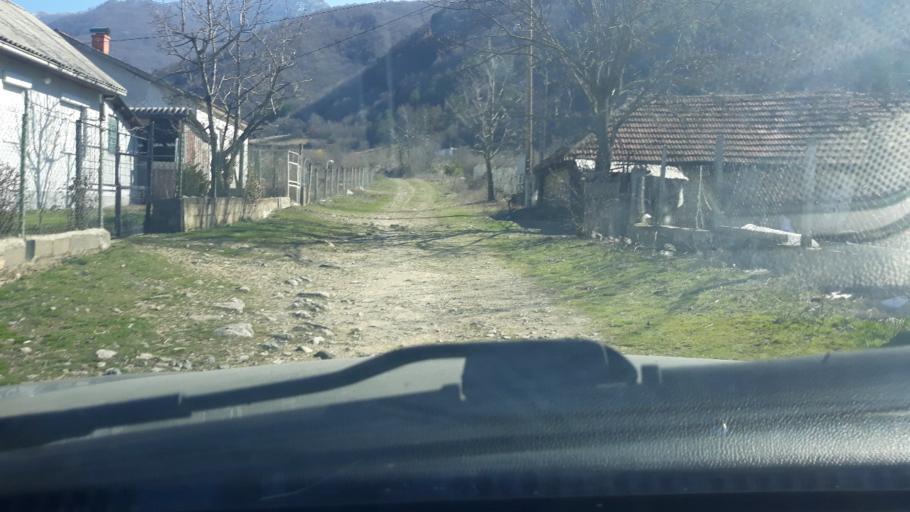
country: MK
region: Novo Selo
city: Susica
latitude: 41.3785
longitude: 22.8183
